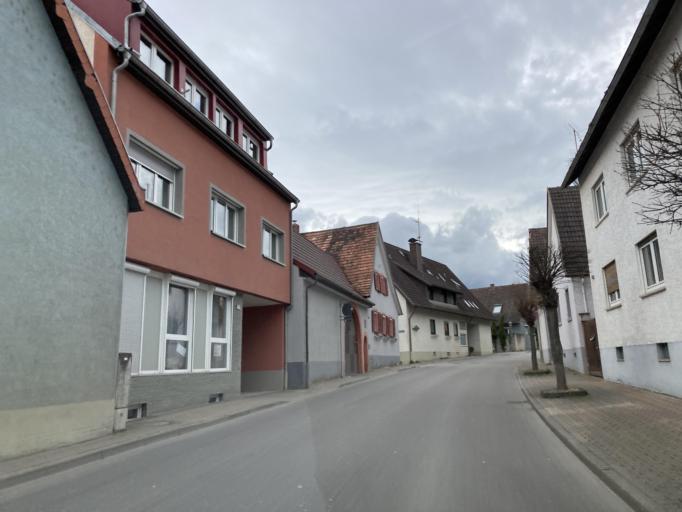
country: DE
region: Baden-Wuerttemberg
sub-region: Freiburg Region
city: Botzingen
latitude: 48.0744
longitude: 7.7065
